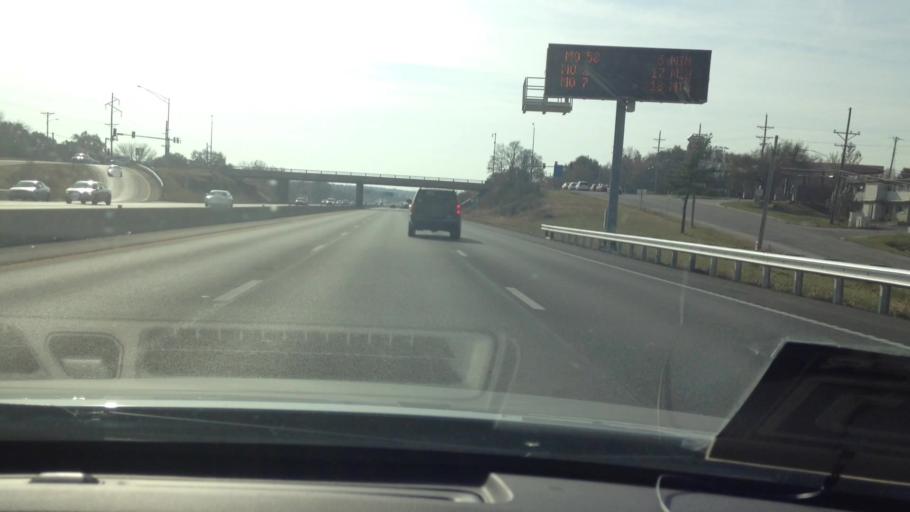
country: US
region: Missouri
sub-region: Jackson County
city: Grandview
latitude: 38.8725
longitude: -94.5265
